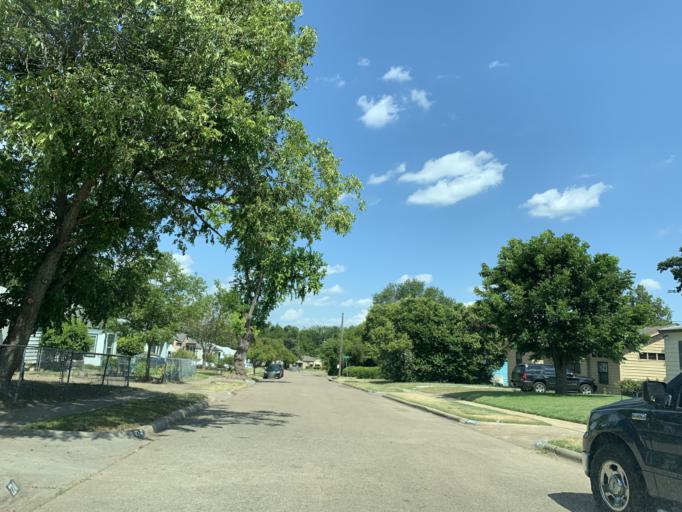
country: US
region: Texas
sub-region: Dallas County
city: Dallas
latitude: 32.7123
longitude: -96.7909
